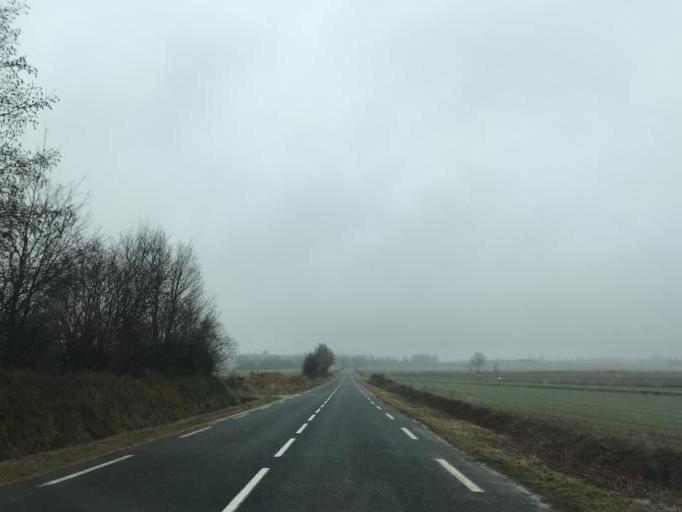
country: FR
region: Rhone-Alpes
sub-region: Departement de l'Ain
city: Miribel
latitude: 45.8447
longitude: 4.9370
